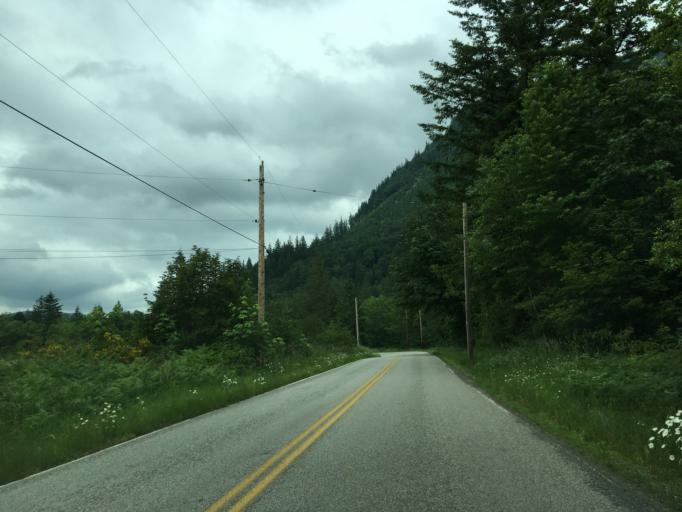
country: US
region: Washington
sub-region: Whatcom County
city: Peaceful Valley
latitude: 48.9861
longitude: -122.0732
